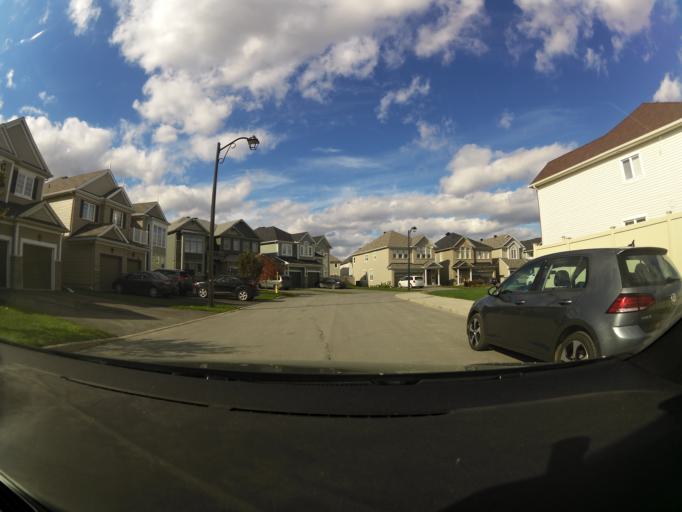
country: CA
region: Ontario
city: Bells Corners
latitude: 45.2717
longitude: -75.8868
